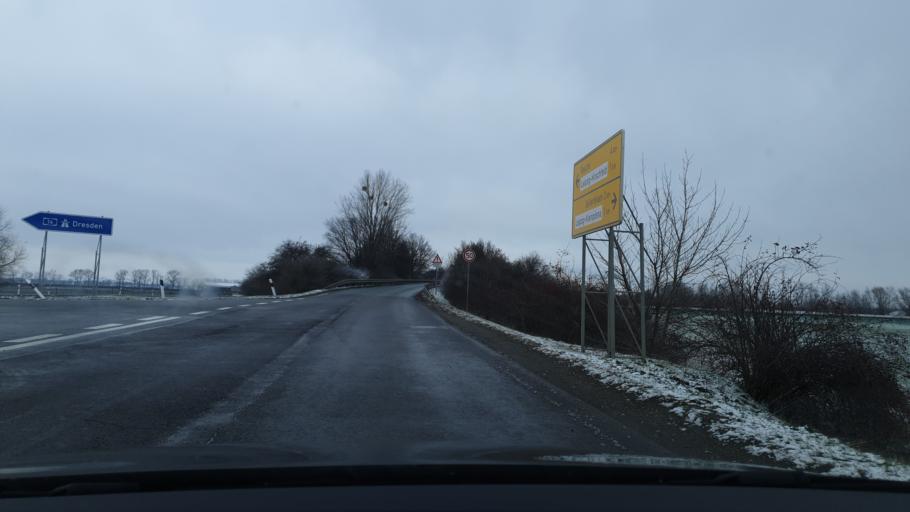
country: DE
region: Saxony
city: Borsdorf
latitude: 51.3166
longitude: 12.5203
